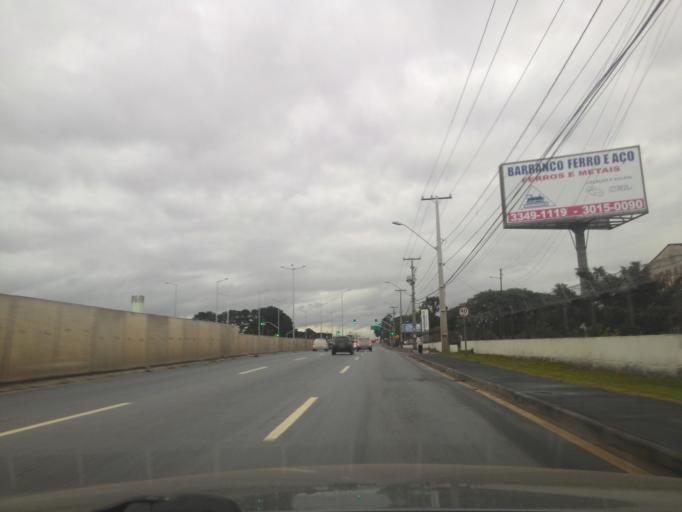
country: BR
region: Parana
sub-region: Sao Jose Dos Pinhais
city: Sao Jose dos Pinhais
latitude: -25.5185
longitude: -49.2923
